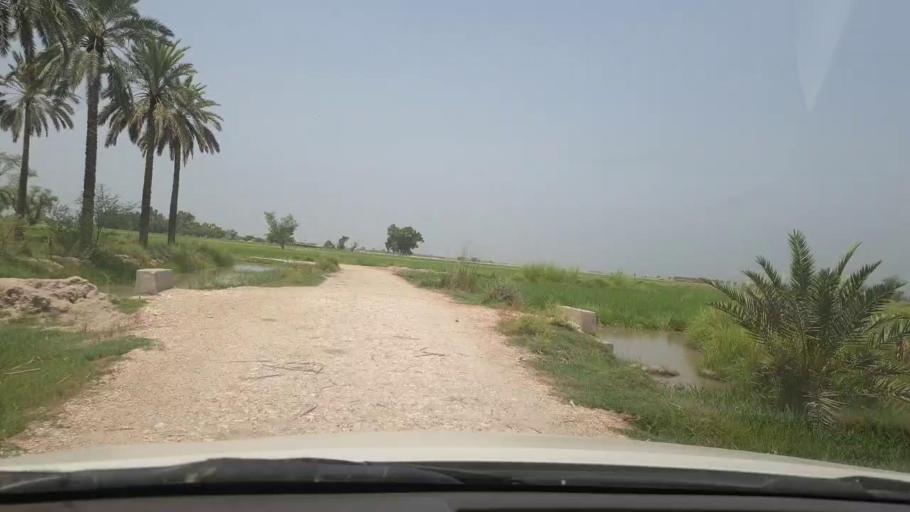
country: PK
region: Sindh
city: Shikarpur
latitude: 28.0180
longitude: 68.6146
